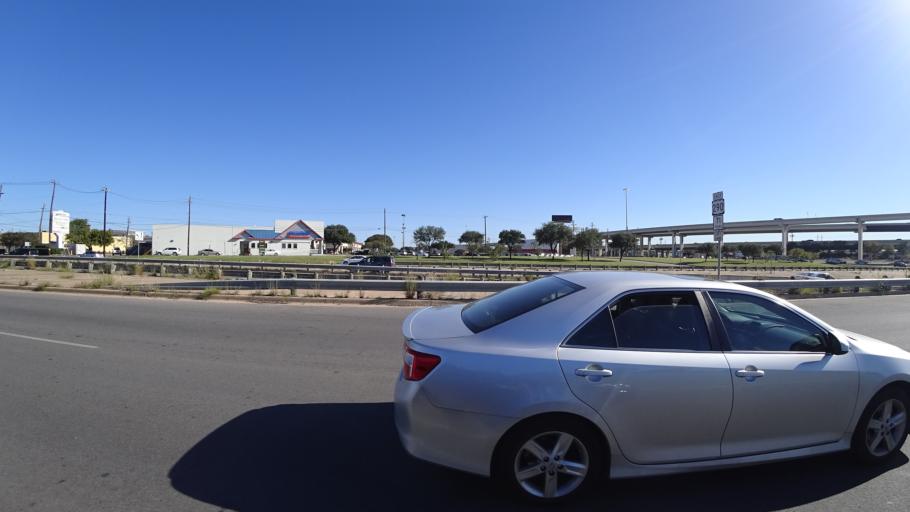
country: US
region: Texas
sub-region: Travis County
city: Rollingwood
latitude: 30.2355
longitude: -97.7943
